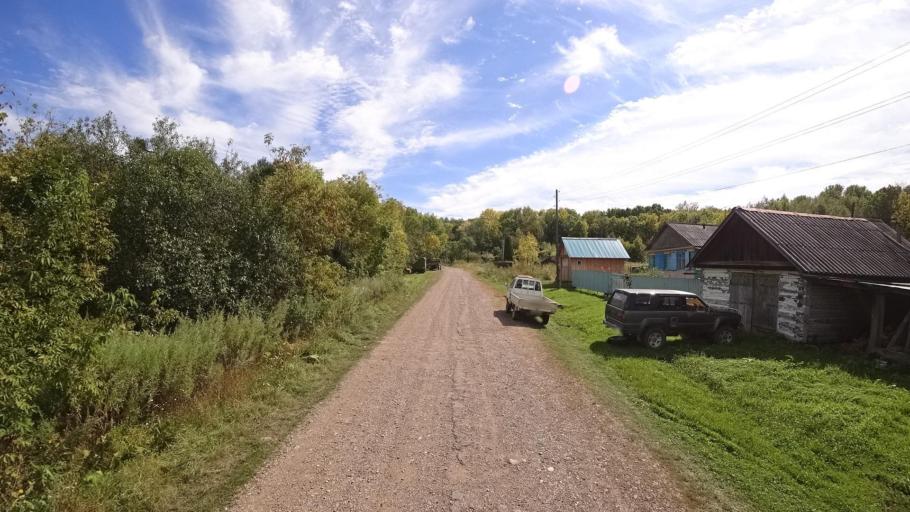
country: RU
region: Primorskiy
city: Yakovlevka
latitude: 44.6533
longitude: 133.7476
